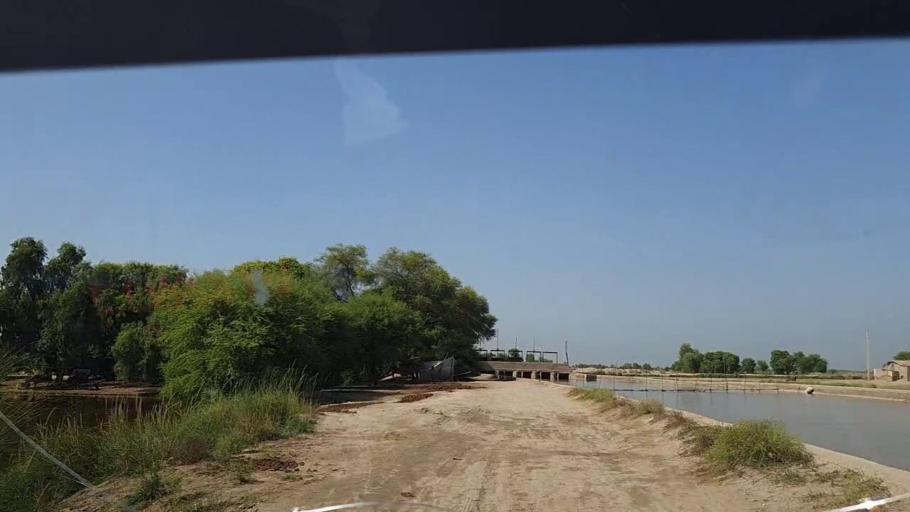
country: PK
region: Sindh
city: Ghauspur
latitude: 28.1744
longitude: 69.0993
